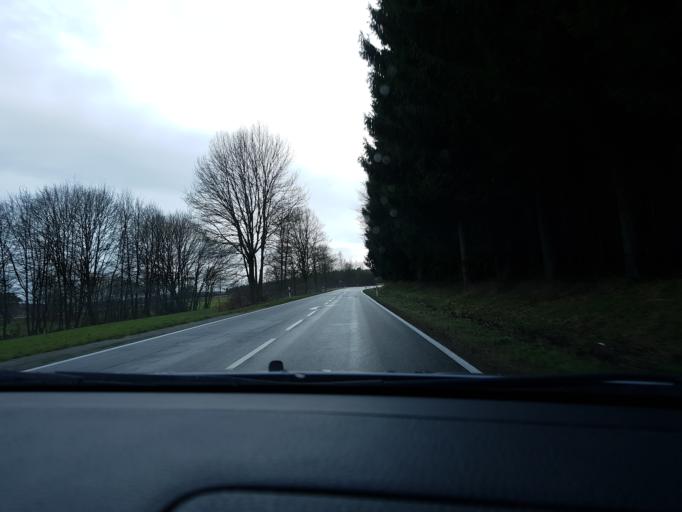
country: DE
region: Rheinland-Pfalz
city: Oberelbert
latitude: 50.3870
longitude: 7.8106
